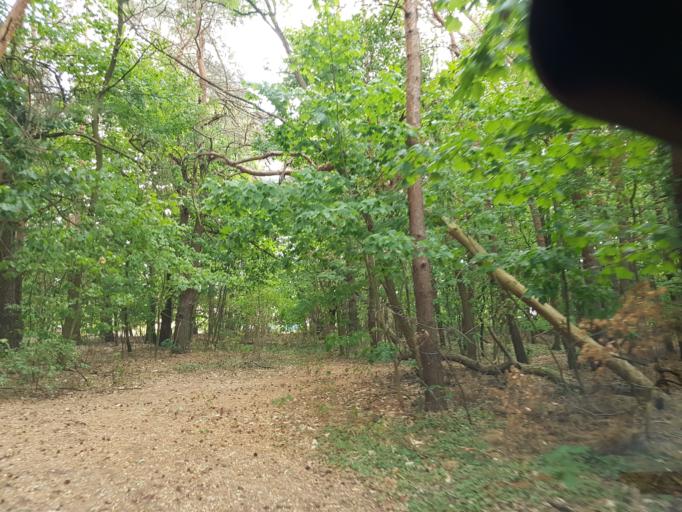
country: DE
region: Brandenburg
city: Niedergorsdorf
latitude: 52.0095
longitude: 13.0005
